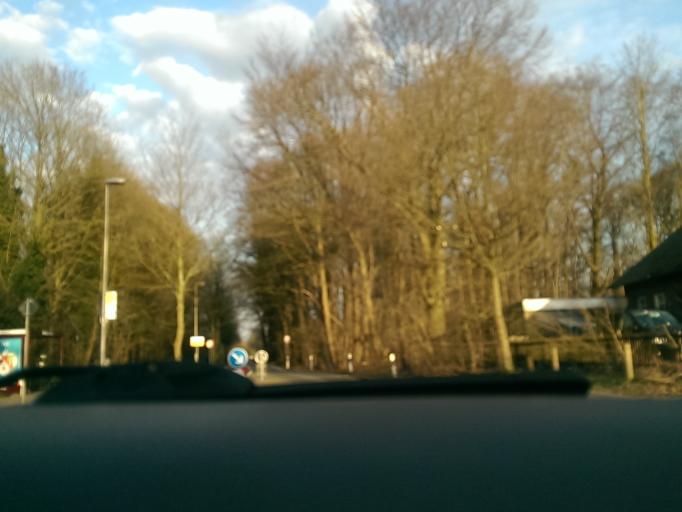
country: DE
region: North Rhine-Westphalia
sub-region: Regierungsbezirk Munster
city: Muenster
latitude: 51.9287
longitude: 7.6834
